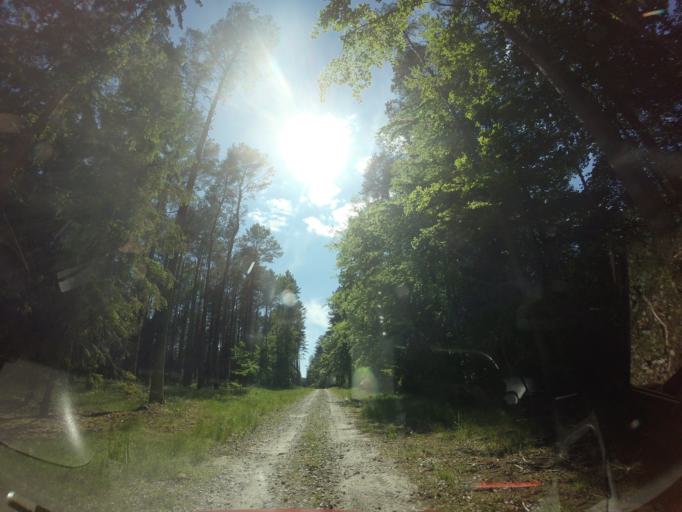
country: PL
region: West Pomeranian Voivodeship
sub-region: Powiat choszczenski
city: Drawno
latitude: 53.1734
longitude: 15.6599
